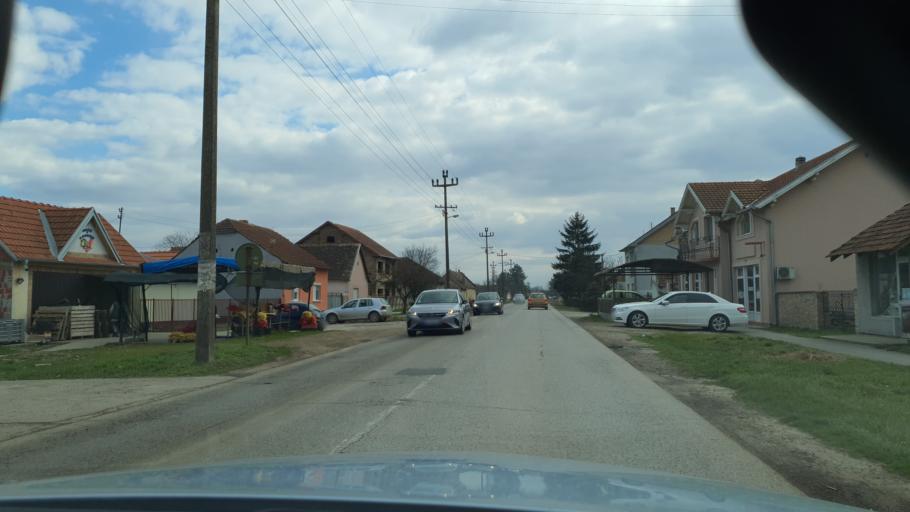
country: RS
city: Maglic
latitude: 45.3912
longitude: 19.4589
